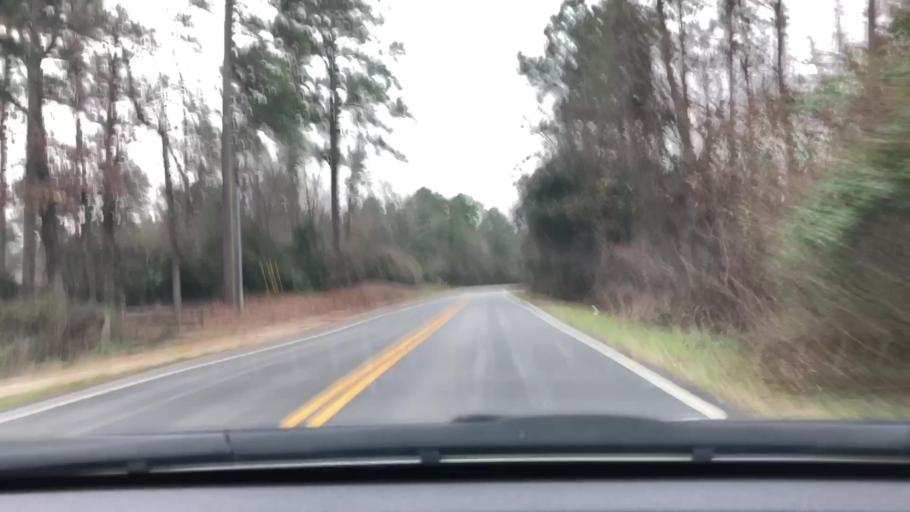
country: US
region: South Carolina
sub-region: Sumter County
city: Cherryvale
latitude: 33.9463
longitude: -80.4032
